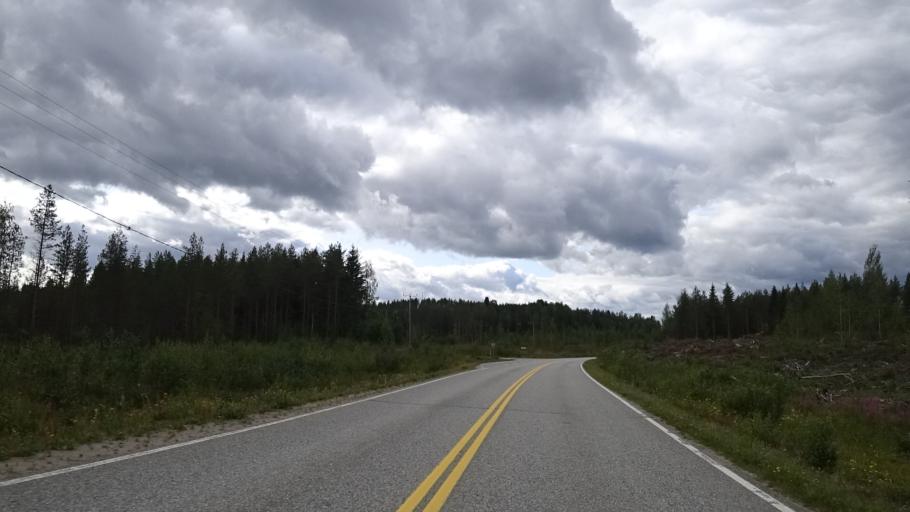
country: FI
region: North Karelia
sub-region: Joensuu
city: Ilomantsi
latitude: 62.6254
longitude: 31.2540
